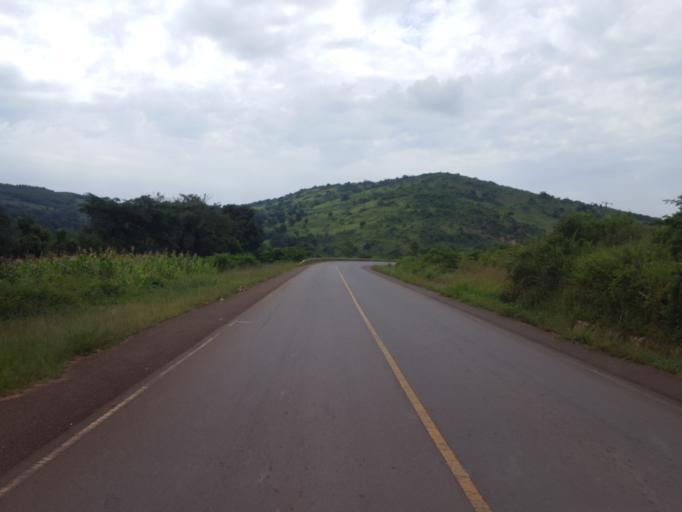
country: UG
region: Central Region
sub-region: Mityana District
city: Mityana
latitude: 0.6249
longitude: 32.1318
